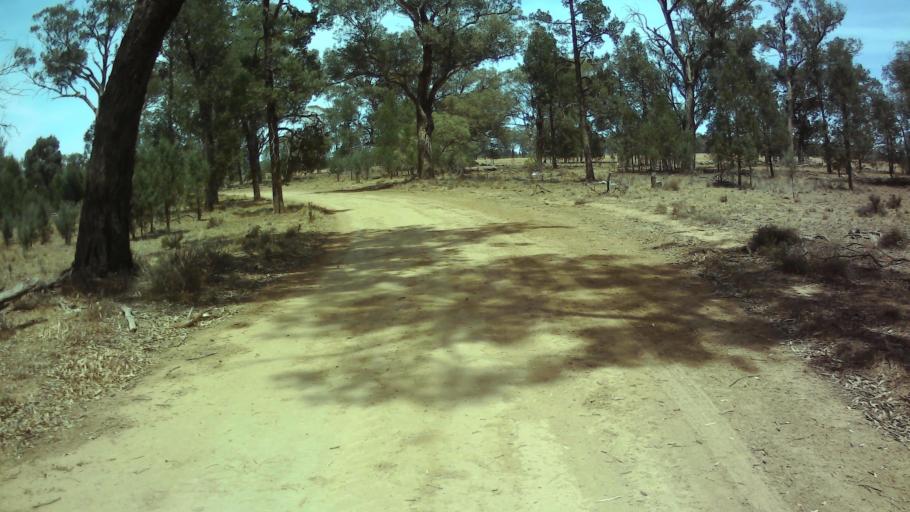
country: AU
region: New South Wales
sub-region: Weddin
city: Grenfell
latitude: -34.0355
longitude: 147.9249
